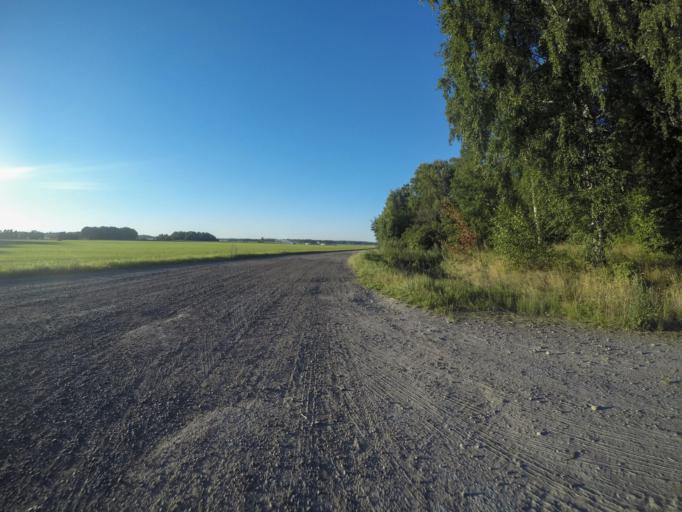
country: SE
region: Vaestmanland
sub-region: Vasteras
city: Vasteras
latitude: 59.5735
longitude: 16.6526
